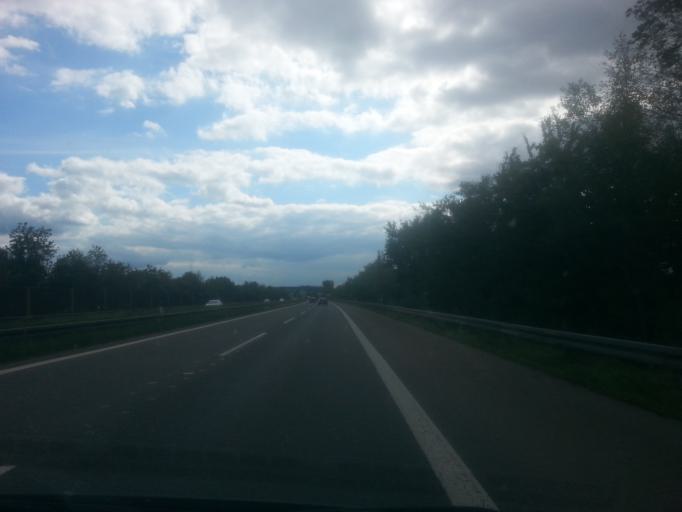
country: DE
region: Bavaria
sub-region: Upper Palatinate
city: Stulln
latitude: 49.4137
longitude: 12.1650
